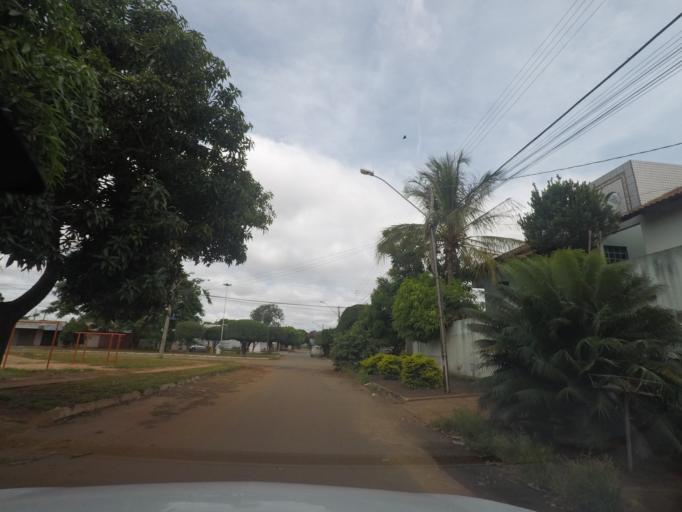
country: BR
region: Goias
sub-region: Goiania
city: Goiania
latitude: -16.6260
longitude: -49.2219
